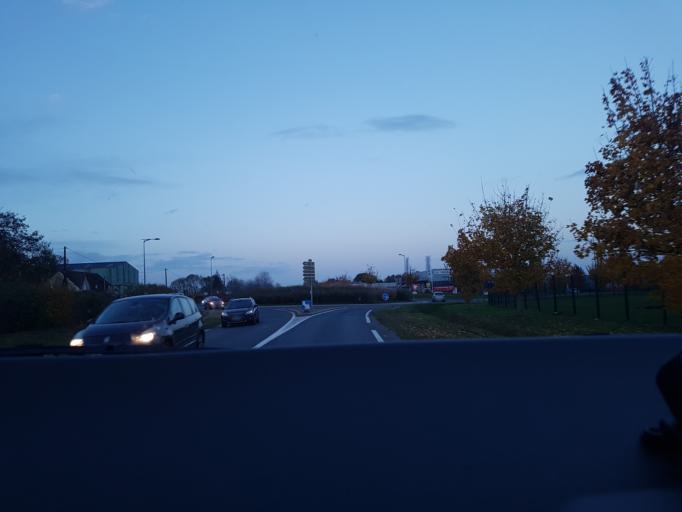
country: FR
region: Haute-Normandie
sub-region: Departement de l'Eure
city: Beuzeville
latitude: 49.3401
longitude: 0.3570
